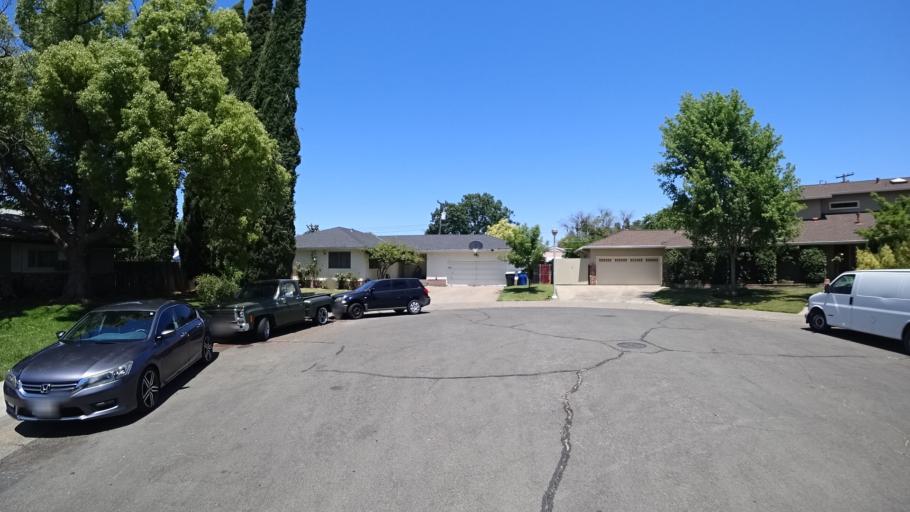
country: US
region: California
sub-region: Sacramento County
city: Parkway
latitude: 38.5326
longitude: -121.4378
